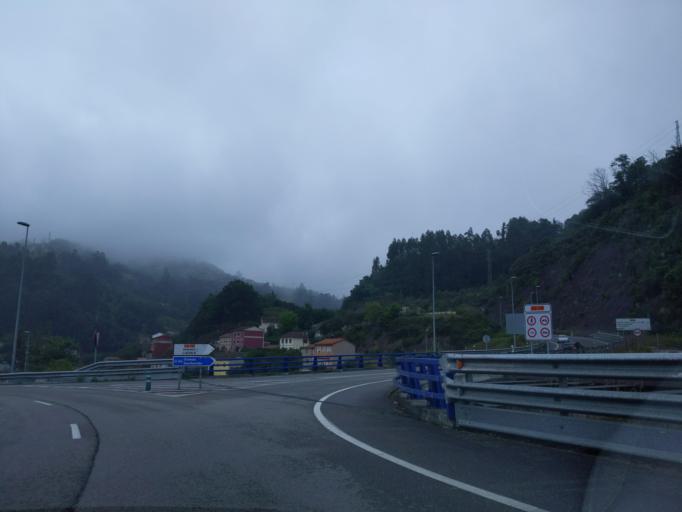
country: ES
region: Asturias
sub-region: Province of Asturias
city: El entrego
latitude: 43.2850
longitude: -5.6229
